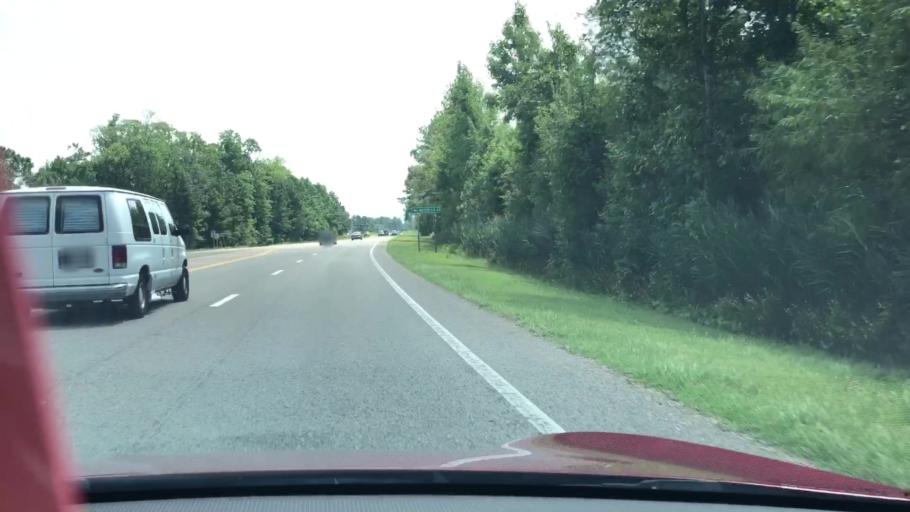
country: US
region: North Carolina
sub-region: Currituck County
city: Currituck
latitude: 36.3357
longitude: -75.9486
